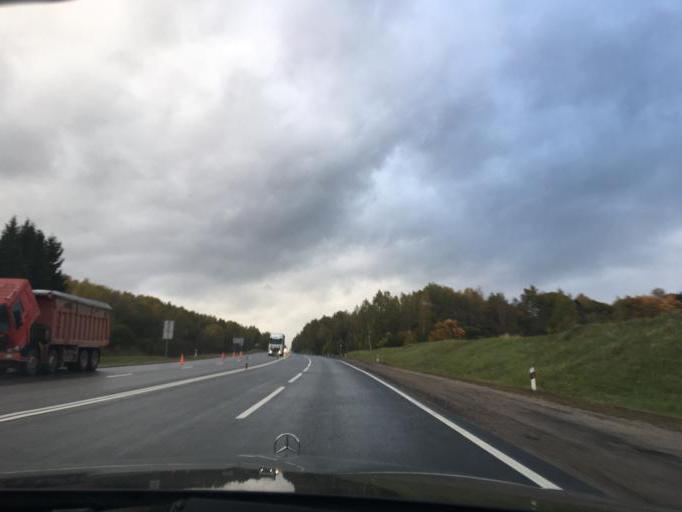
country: RU
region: Smolensk
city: Pechersk
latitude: 54.8976
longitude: 32.1182
